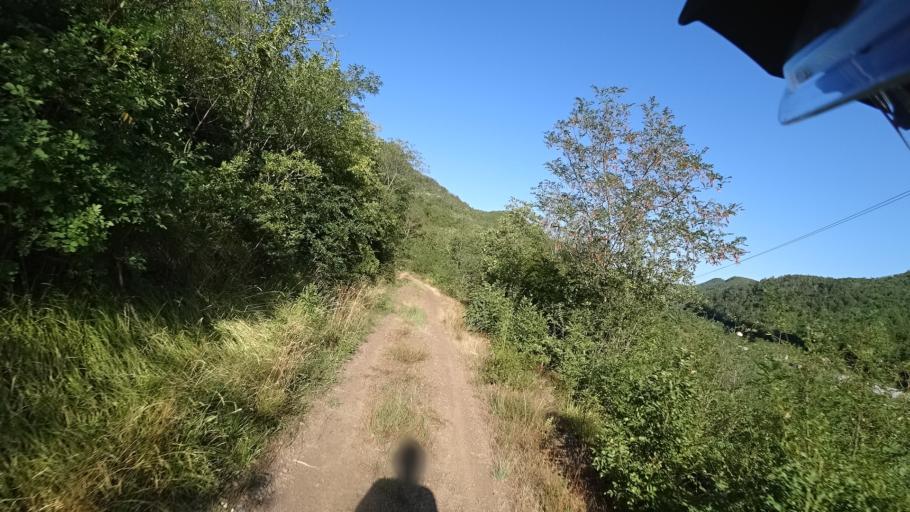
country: HR
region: Sibensko-Kniniska
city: Knin
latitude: 44.1169
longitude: 16.2044
